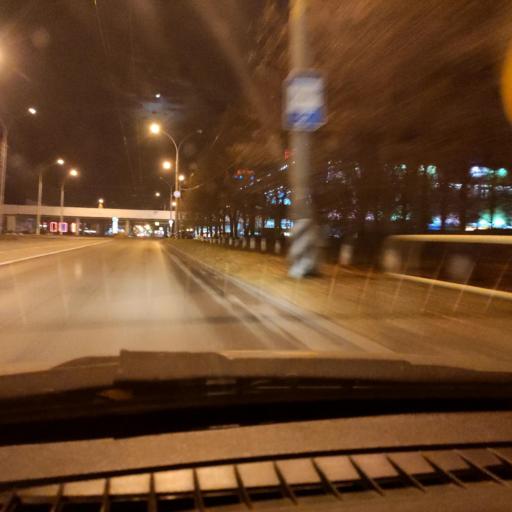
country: RU
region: Samara
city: Tol'yatti
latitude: 53.5194
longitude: 49.2739
